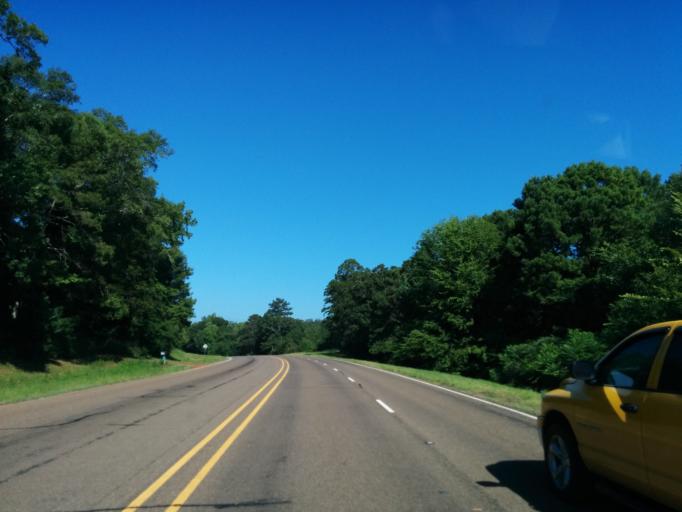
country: US
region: Texas
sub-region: Sabine County
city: Milam
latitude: 31.4311
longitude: -93.8175
